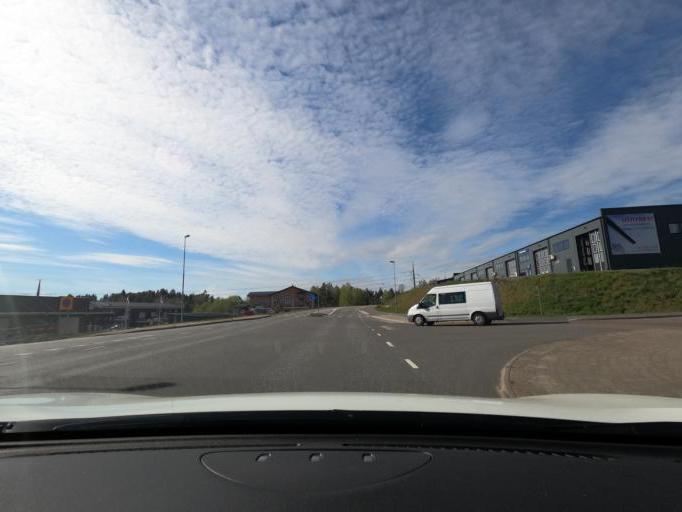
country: SE
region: Vaestra Goetaland
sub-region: Harryda Kommun
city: Landvetter
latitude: 57.6768
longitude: 12.2420
